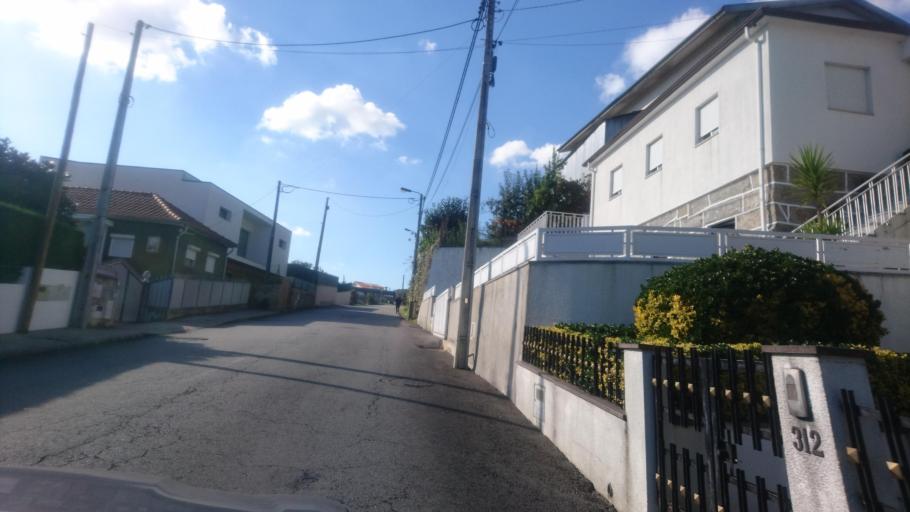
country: PT
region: Porto
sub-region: Paredes
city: Madalena
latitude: 41.2314
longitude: -8.3521
